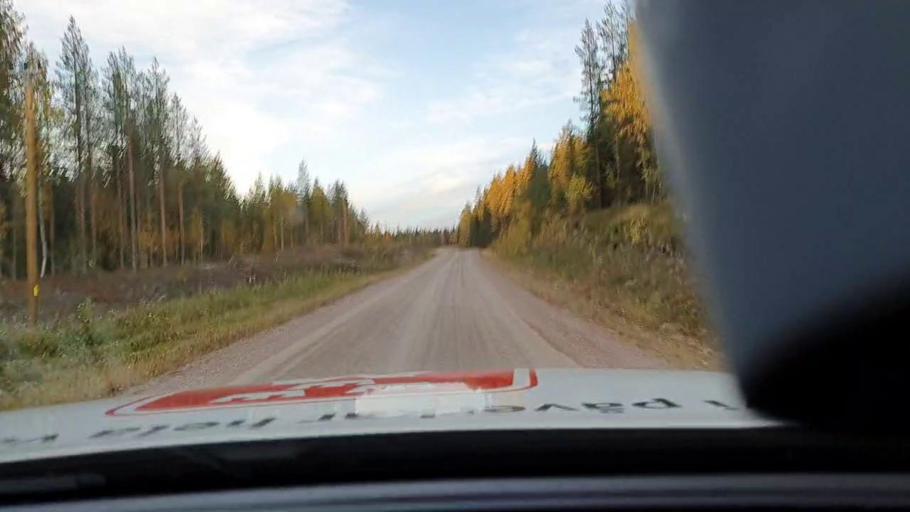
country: SE
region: Norrbotten
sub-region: Overkalix Kommun
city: OEverkalix
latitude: 66.3238
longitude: 22.6291
